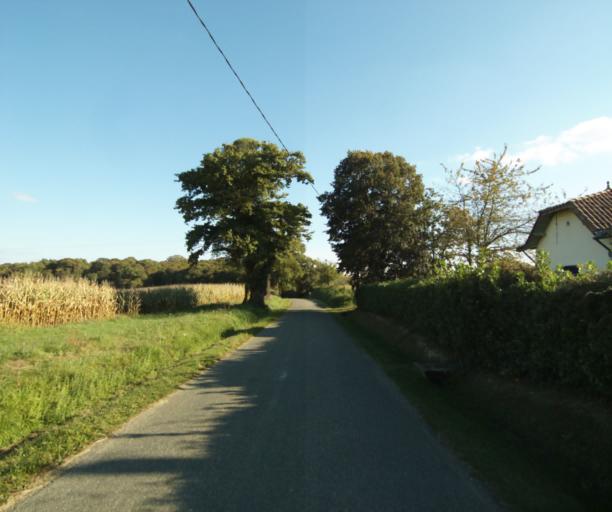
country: FR
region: Midi-Pyrenees
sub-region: Departement du Gers
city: Eauze
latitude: 43.7936
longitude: 0.1365
